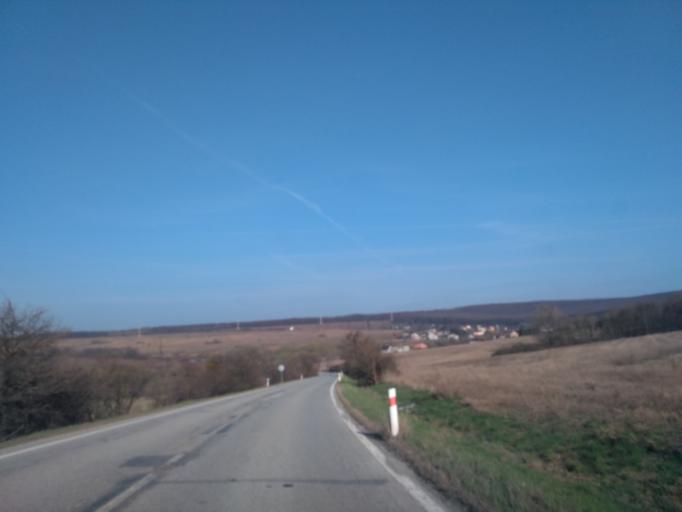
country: SK
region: Kosicky
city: Kosice
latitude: 48.6808
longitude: 21.2017
